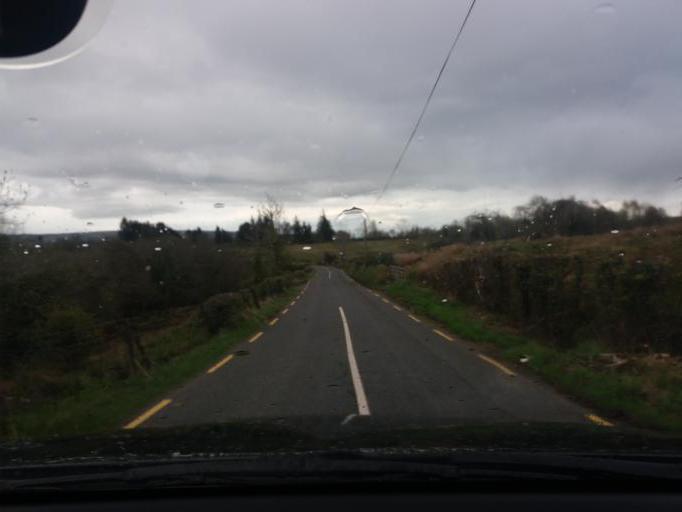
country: IE
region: Ulster
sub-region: An Cabhan
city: Ballyconnell
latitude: 54.1572
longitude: -7.7588
